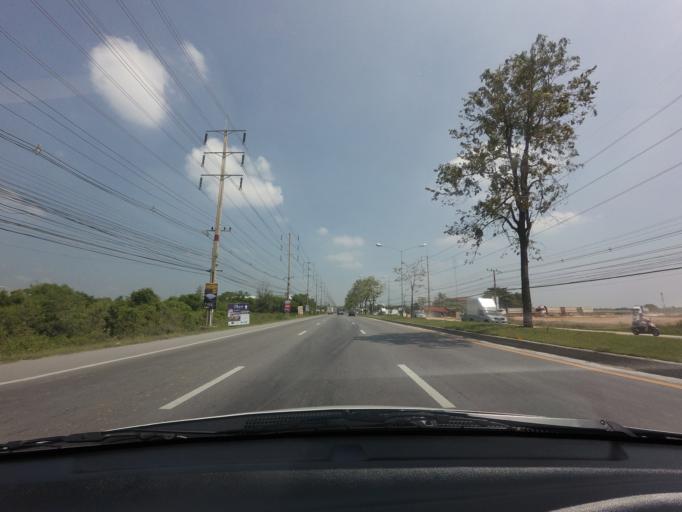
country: TH
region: Chachoengsao
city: Bang Pakong
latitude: 13.5829
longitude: 101.0086
